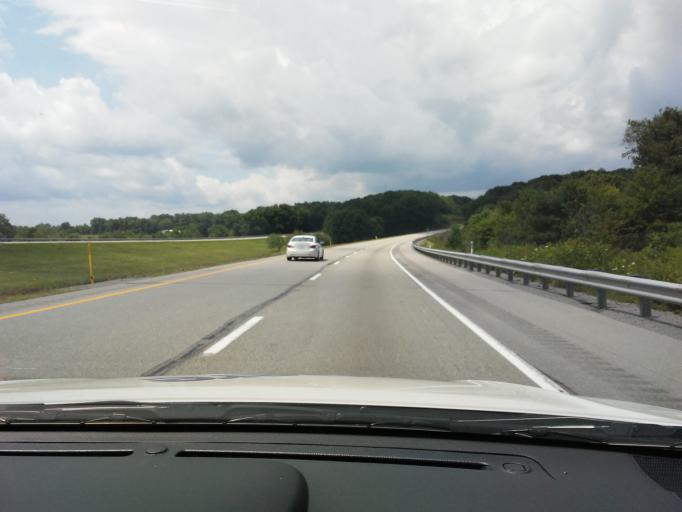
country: US
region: Pennsylvania
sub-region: Clearfield County
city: Troy
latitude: 40.9809
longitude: -78.1362
